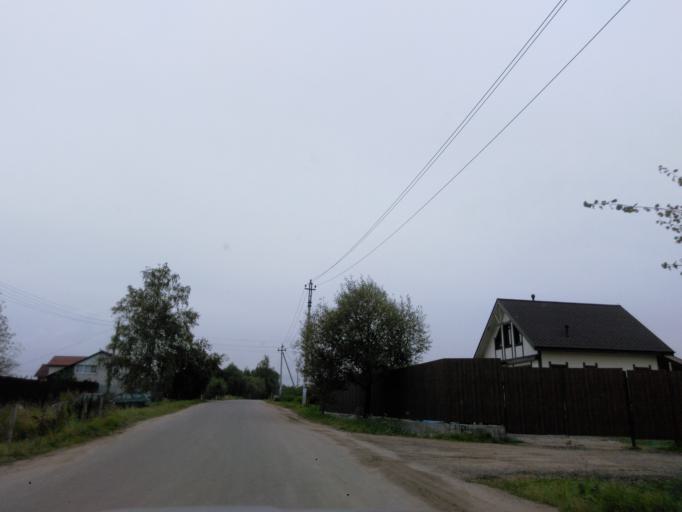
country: RU
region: Moskovskaya
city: Mendeleyevo
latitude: 56.0972
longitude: 37.2704
